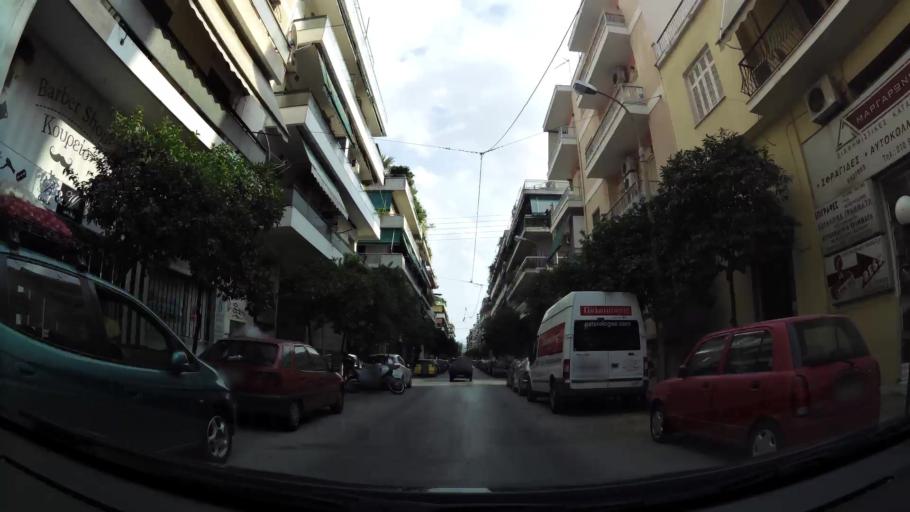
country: GR
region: Attica
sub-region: Nomarchia Athinas
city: Kallithea
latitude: 37.9585
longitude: 23.7079
